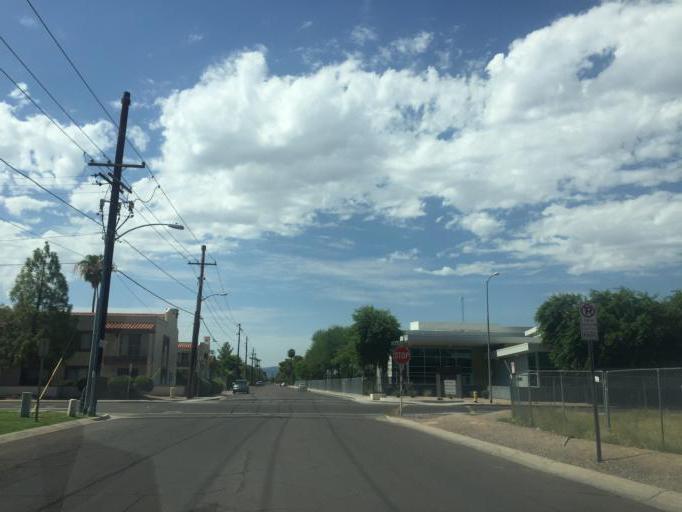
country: US
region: Arizona
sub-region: Maricopa County
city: Phoenix
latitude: 33.5313
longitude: -112.0606
